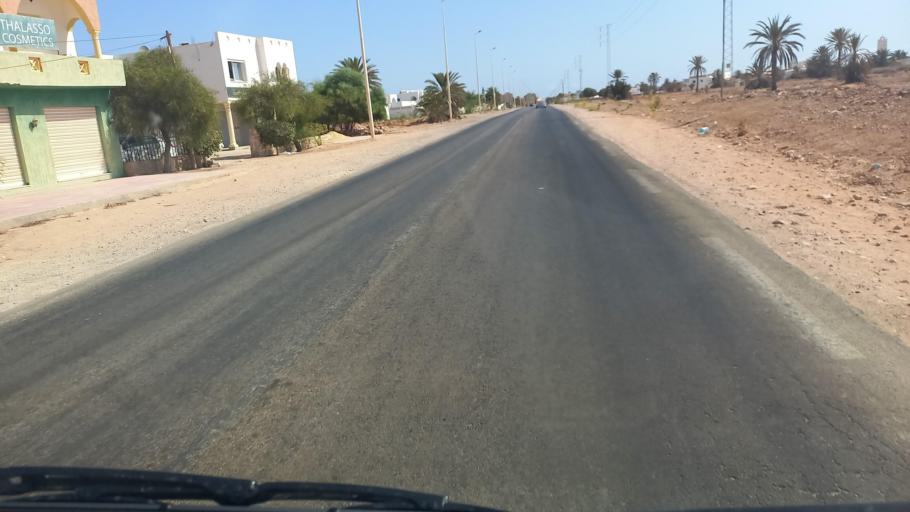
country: TN
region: Madanin
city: Midoun
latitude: 33.7619
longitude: 11.0128
